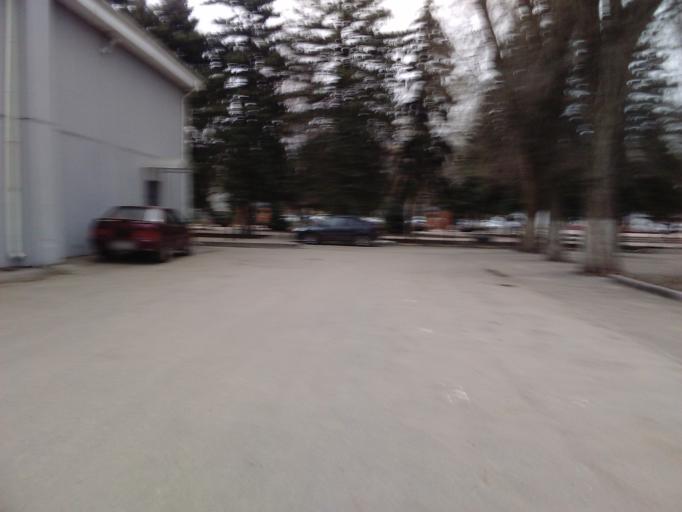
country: RU
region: Rostov
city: Bataysk
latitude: 47.1366
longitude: 39.7435
